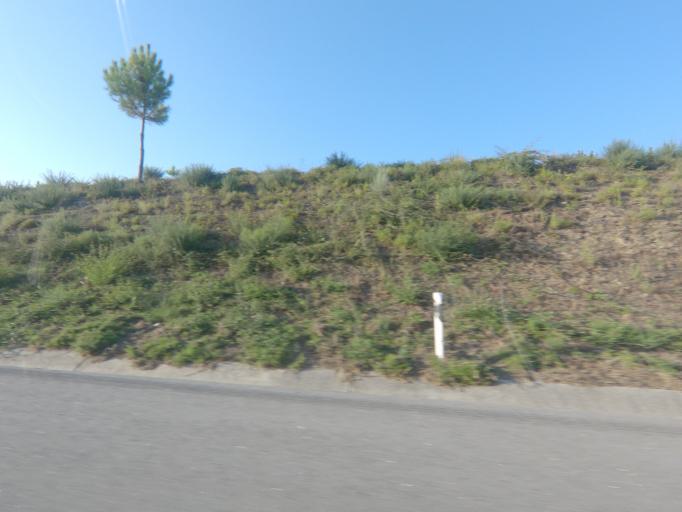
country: PT
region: Vila Real
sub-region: Sabrosa
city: Vilela
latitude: 41.2644
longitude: -7.6284
